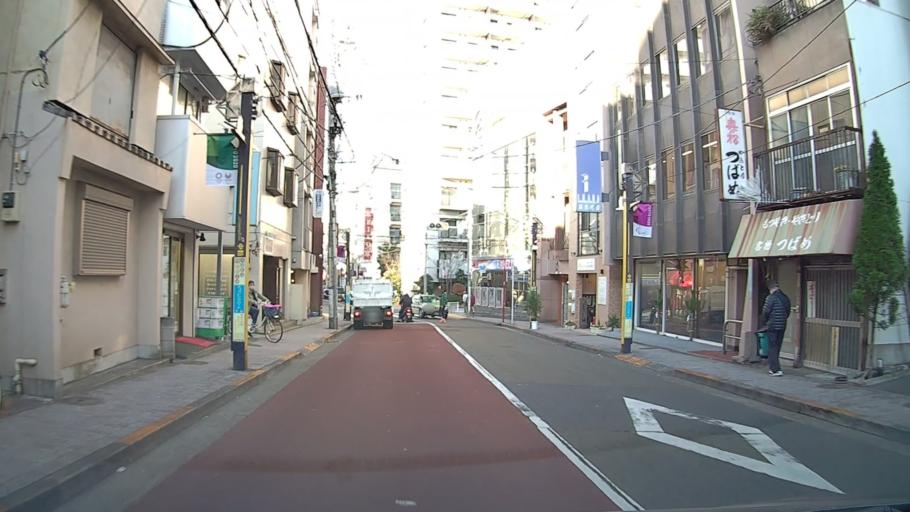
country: JP
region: Tokyo
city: Tokyo
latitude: 35.6911
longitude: 139.6743
